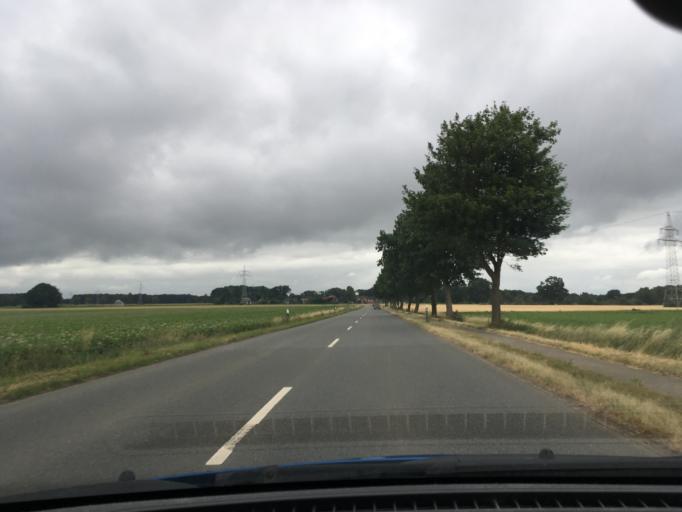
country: DE
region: Lower Saxony
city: Soderstorf
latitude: 53.1661
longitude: 10.1583
